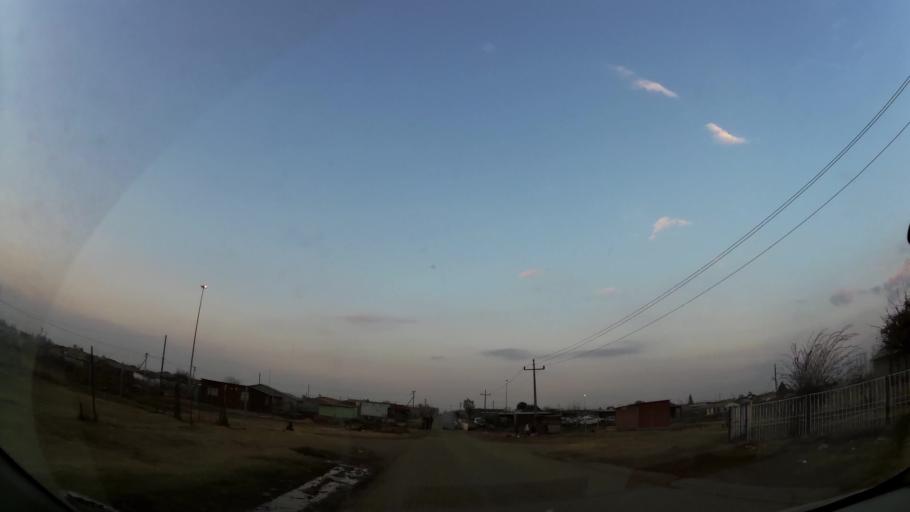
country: ZA
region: Gauteng
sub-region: City of Johannesburg Metropolitan Municipality
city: Orange Farm
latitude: -26.5531
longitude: 27.8717
